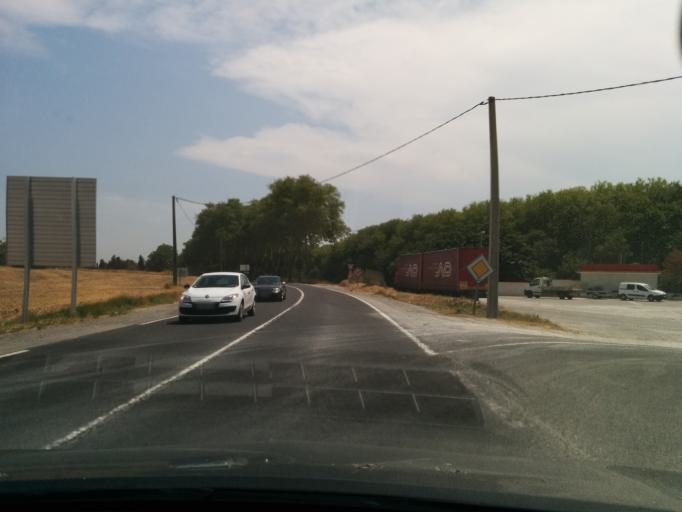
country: FR
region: Languedoc-Roussillon
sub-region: Departement de l'Aude
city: Castelnaudary
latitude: 43.3045
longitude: 1.9813
